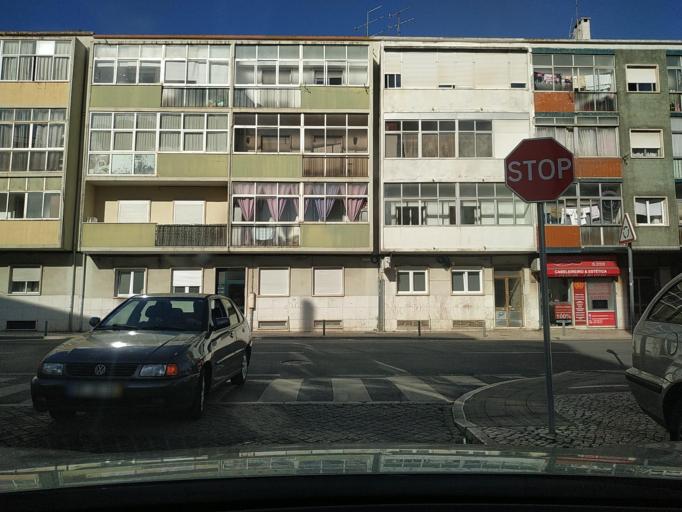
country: PT
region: Lisbon
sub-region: Amadora
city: Amadora
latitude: 38.7603
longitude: -9.2303
